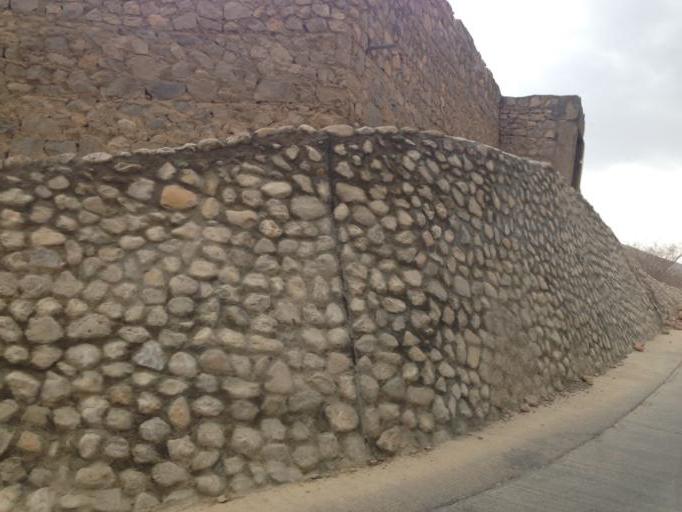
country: OM
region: Ash Sharqiyah
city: Badiyah
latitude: 22.6058
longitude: 59.0867
